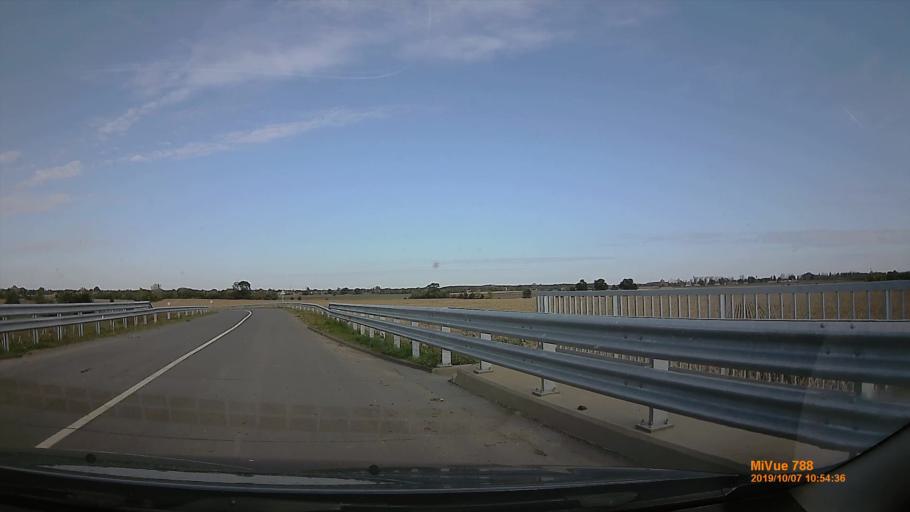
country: HU
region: Bekes
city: Kondoros
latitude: 46.7383
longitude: 20.8083
